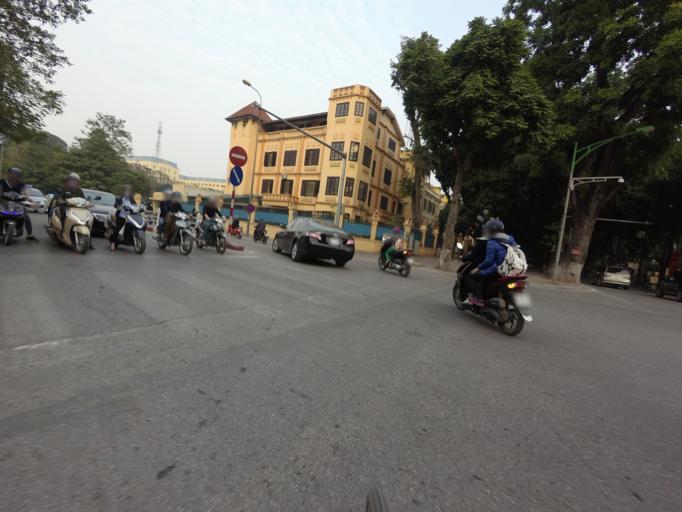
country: VN
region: Ha Noi
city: Hanoi
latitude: 21.0418
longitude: 105.8362
